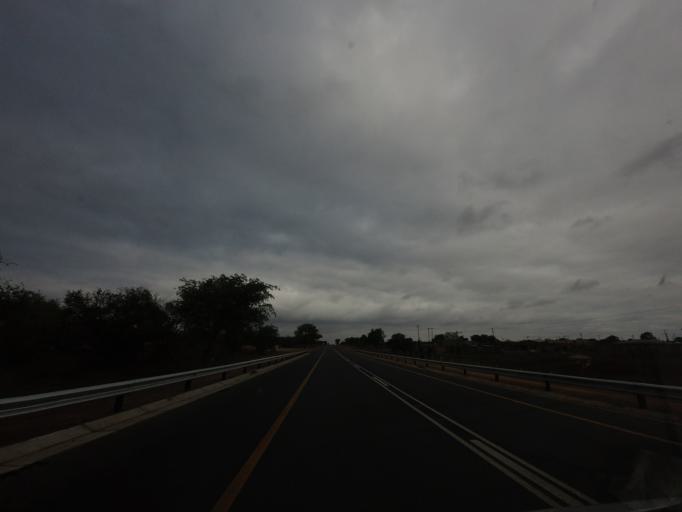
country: ZA
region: Mpumalanga
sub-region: Ehlanzeni District
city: Komatipoort
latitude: -25.4419
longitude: 31.7058
